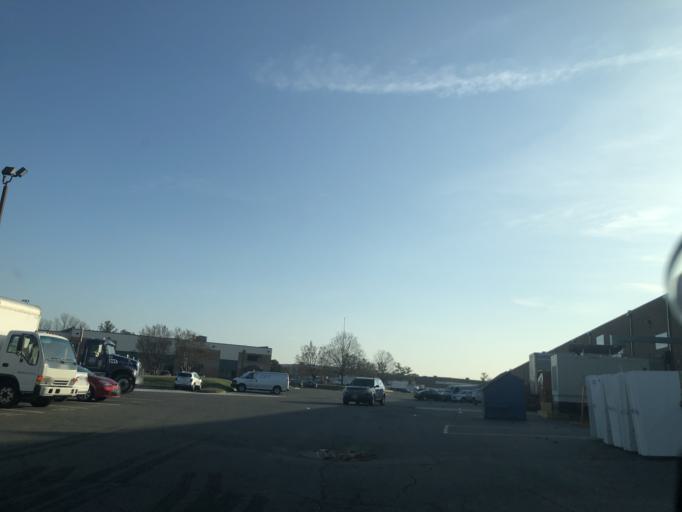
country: US
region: Virginia
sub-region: Fairfax County
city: Floris
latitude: 38.9365
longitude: -77.4263
